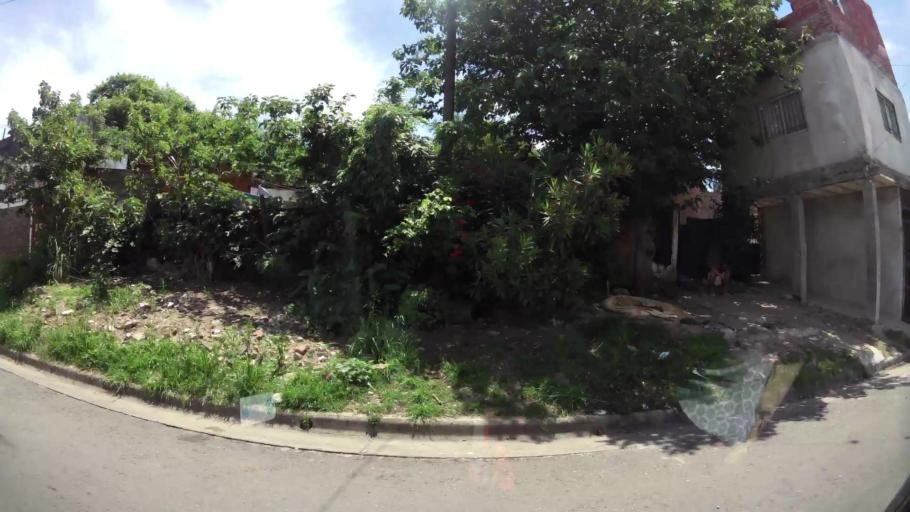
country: AR
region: Santa Fe
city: Gobernador Galvez
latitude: -32.9963
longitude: -60.6207
